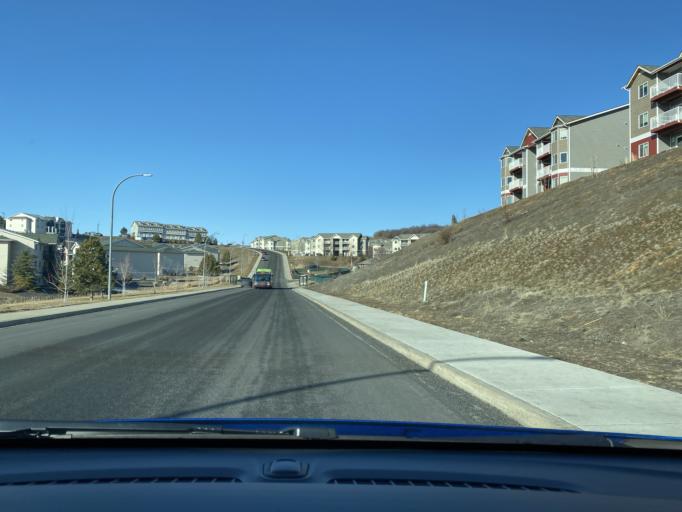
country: US
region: Washington
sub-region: Whitman County
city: Pullman
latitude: 46.7482
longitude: -117.1463
